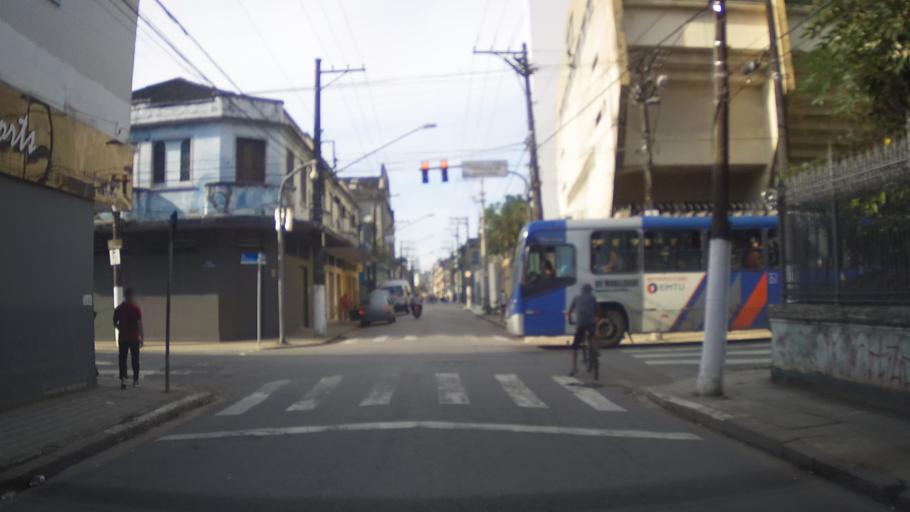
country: BR
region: Sao Paulo
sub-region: Santos
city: Santos
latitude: -23.9400
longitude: -46.3229
